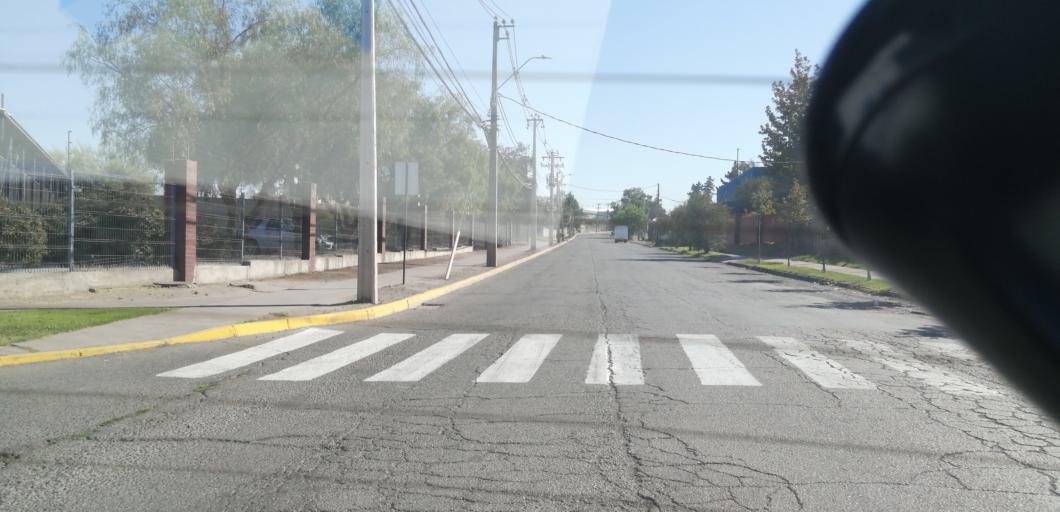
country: CL
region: Santiago Metropolitan
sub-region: Provincia de Santiago
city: Lo Prado
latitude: -33.4506
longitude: -70.7841
